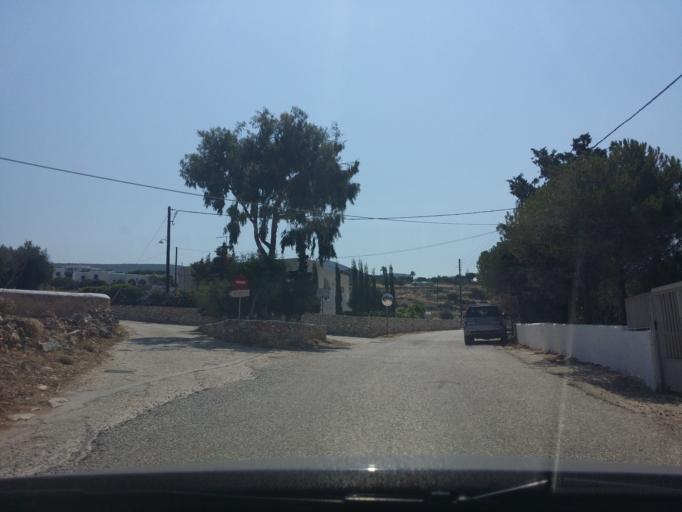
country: GR
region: South Aegean
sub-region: Nomos Kykladon
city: Antiparos
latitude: 36.9986
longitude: 25.1428
